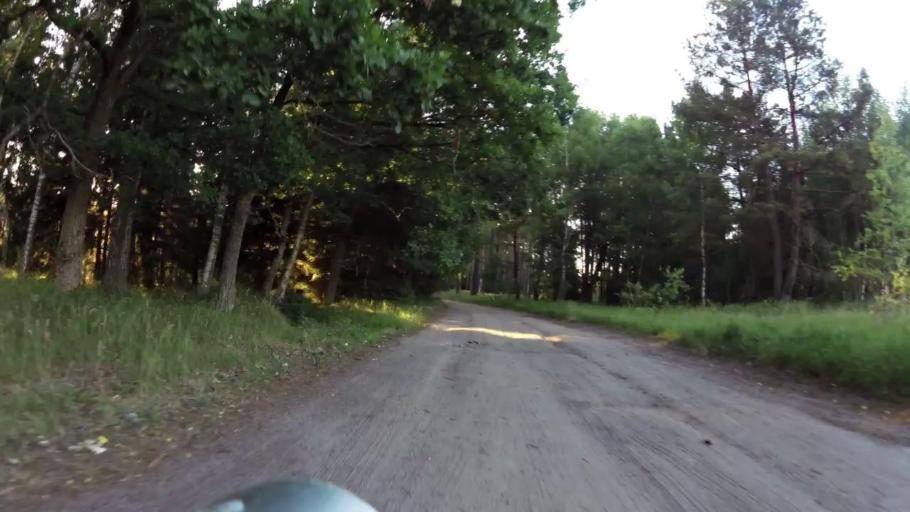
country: PL
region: West Pomeranian Voivodeship
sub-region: Powiat szczecinecki
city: Szczecinek
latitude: 53.8164
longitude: 16.6973
